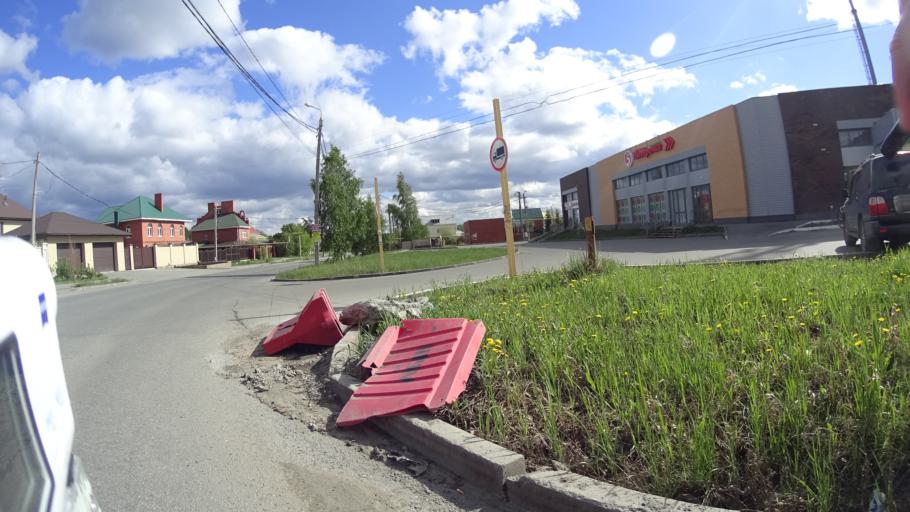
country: RU
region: Chelyabinsk
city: Sargazy
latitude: 55.1544
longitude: 61.2544
